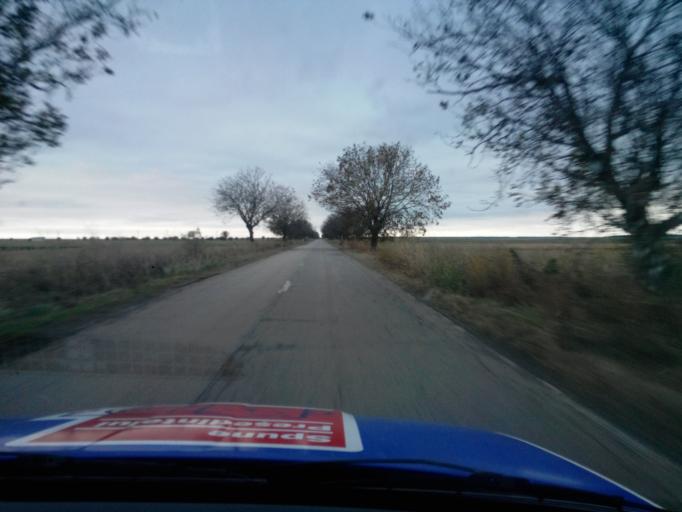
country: RO
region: Giurgiu
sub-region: Comuna Greaca
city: Greaca
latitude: 44.1046
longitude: 26.3007
